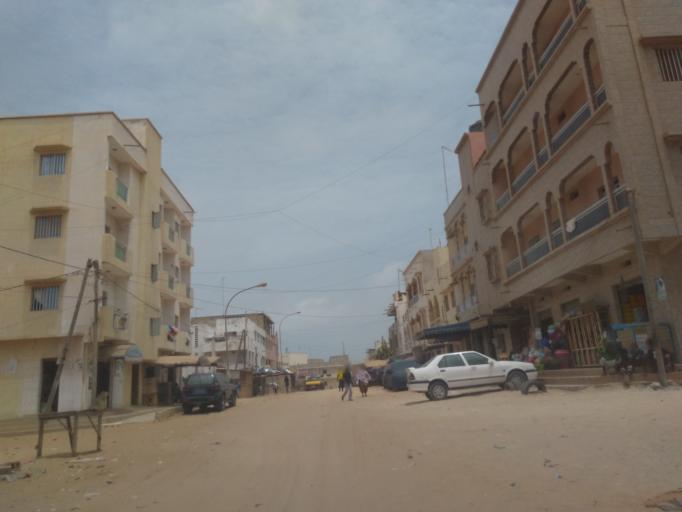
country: SN
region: Dakar
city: Pikine
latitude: 14.7703
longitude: -17.4211
